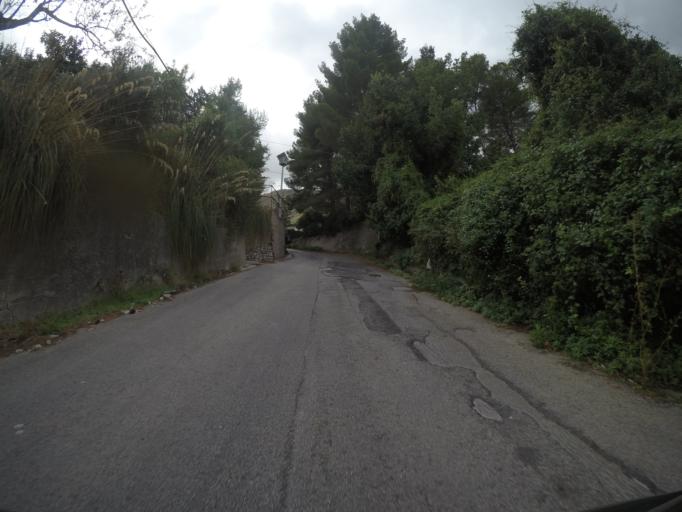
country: IT
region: Sicily
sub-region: Palermo
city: Carini
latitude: 38.1245
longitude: 13.1831
